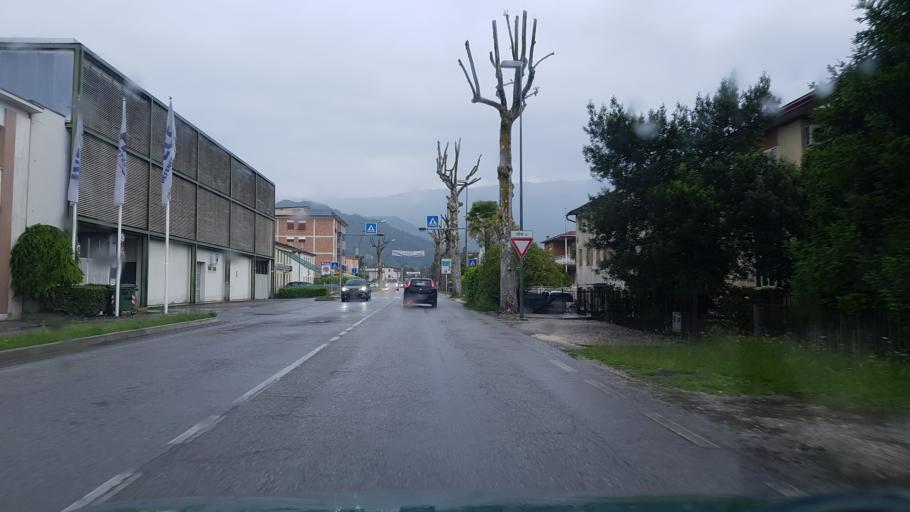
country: IT
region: Veneto
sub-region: Provincia di Treviso
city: Vittorio Veneto
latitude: 45.9698
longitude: 12.3139
